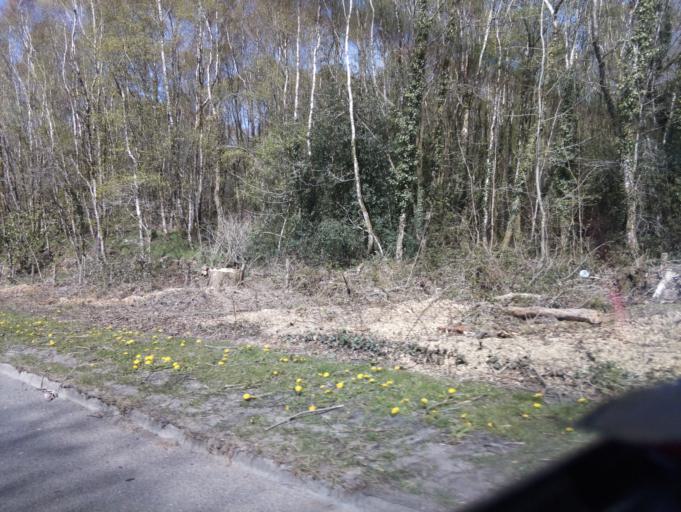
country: GB
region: Wales
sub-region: Rhondda Cynon Taf
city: Cwmbach
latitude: 51.6969
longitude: -3.4080
